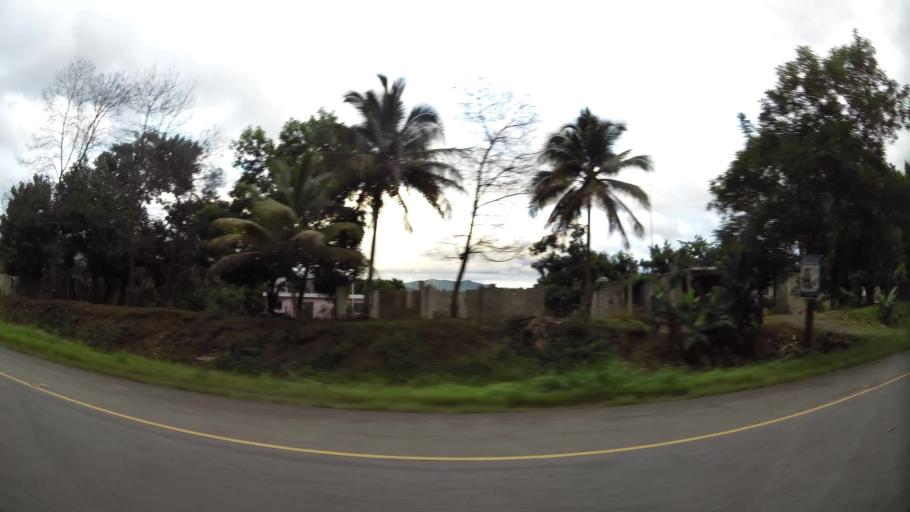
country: DO
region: San Cristobal
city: Villa Altagracia
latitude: 18.6419
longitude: -70.1686
